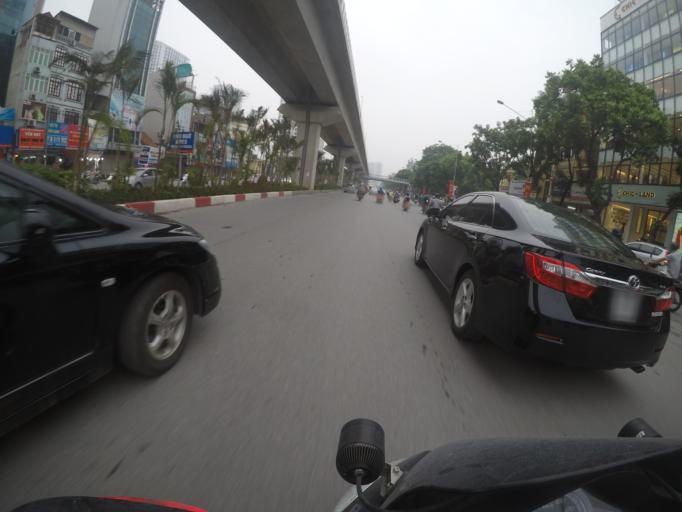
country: VN
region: Ha Noi
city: Thanh Xuan
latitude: 20.9988
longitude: 105.8141
